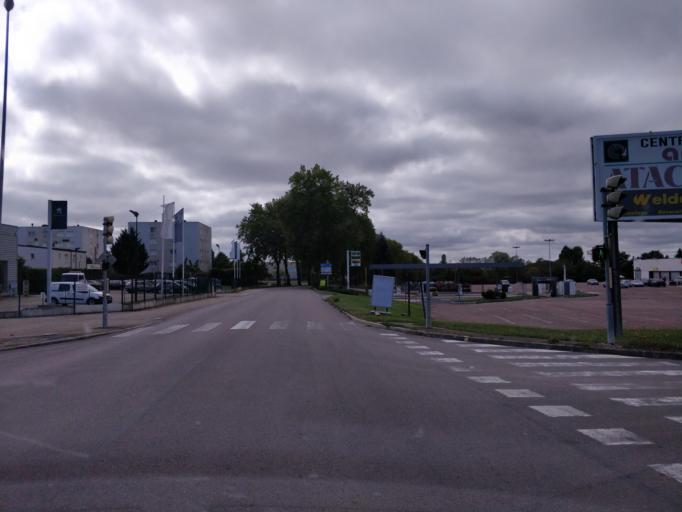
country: FR
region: Bourgogne
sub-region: Departement de l'Yonne
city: Saint-Florentin
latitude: 48.0007
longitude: 3.7200
